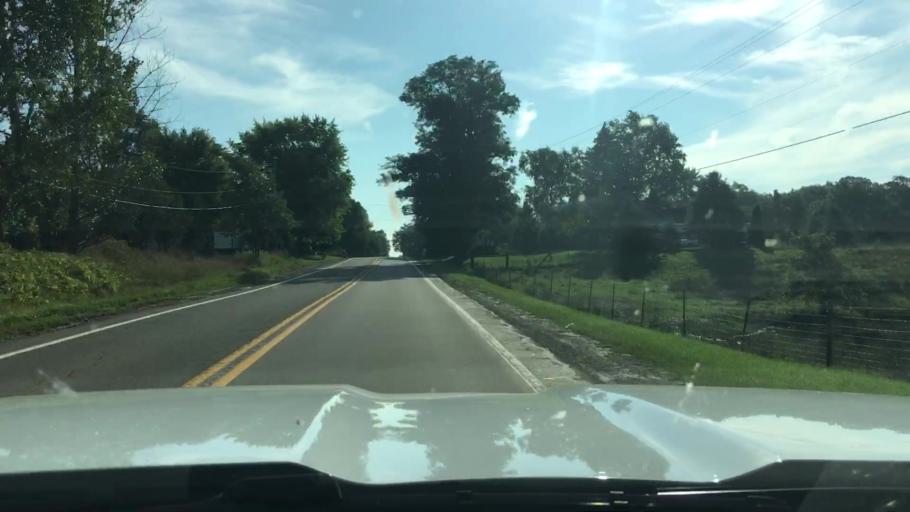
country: US
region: Michigan
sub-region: Kent County
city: Cedar Springs
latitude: 43.2194
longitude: -85.6238
